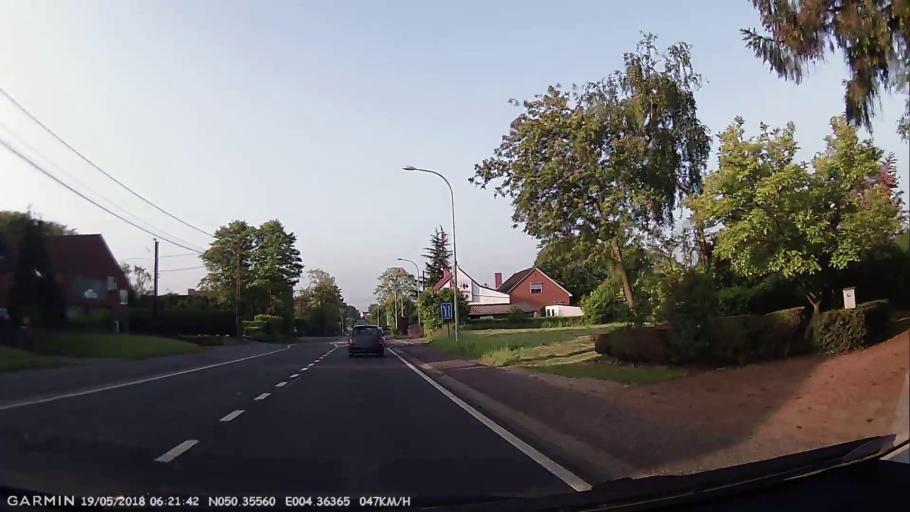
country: BE
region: Wallonia
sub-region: Province du Hainaut
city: Thuin
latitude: 50.3555
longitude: 4.3637
